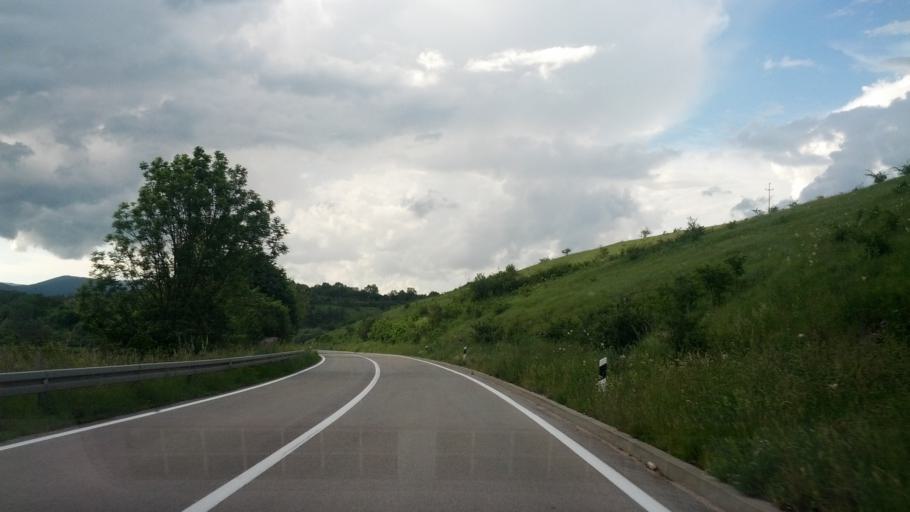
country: BA
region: Federation of Bosnia and Herzegovina
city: Izacic
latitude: 44.9151
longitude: 15.7176
